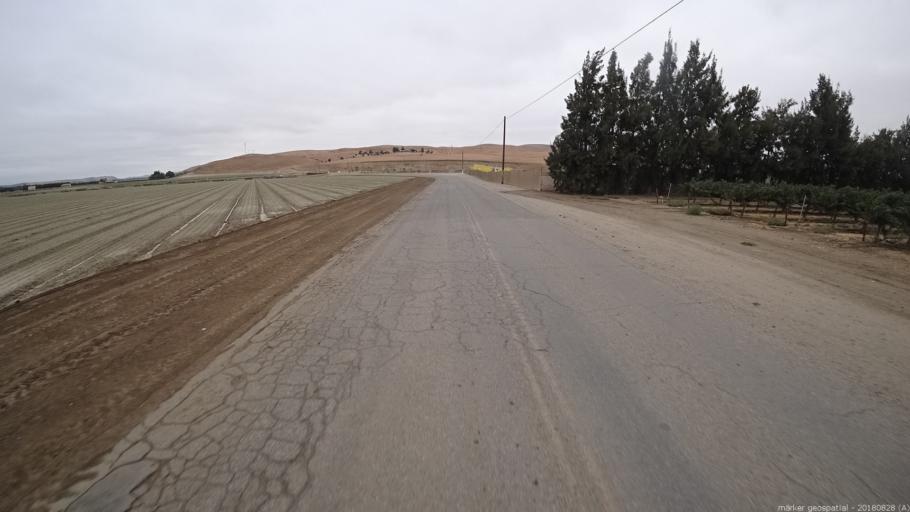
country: US
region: California
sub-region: San Luis Obispo County
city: Lake Nacimiento
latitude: 36.0172
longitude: -120.8863
